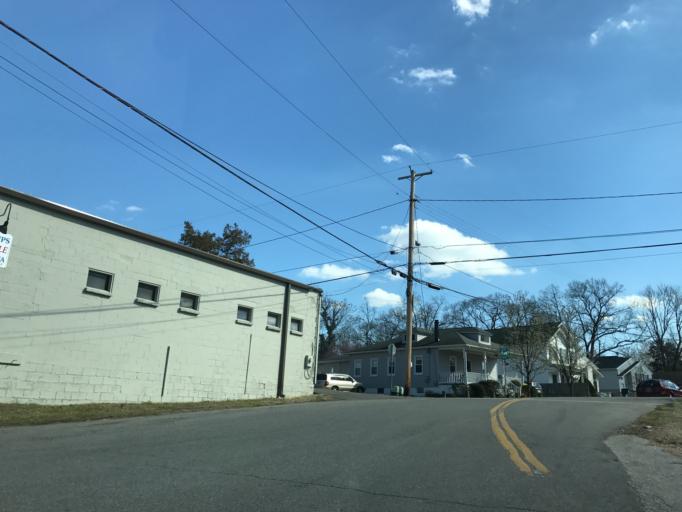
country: US
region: Maryland
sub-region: Anne Arundel County
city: Green Haven
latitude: 39.1452
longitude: -76.5505
